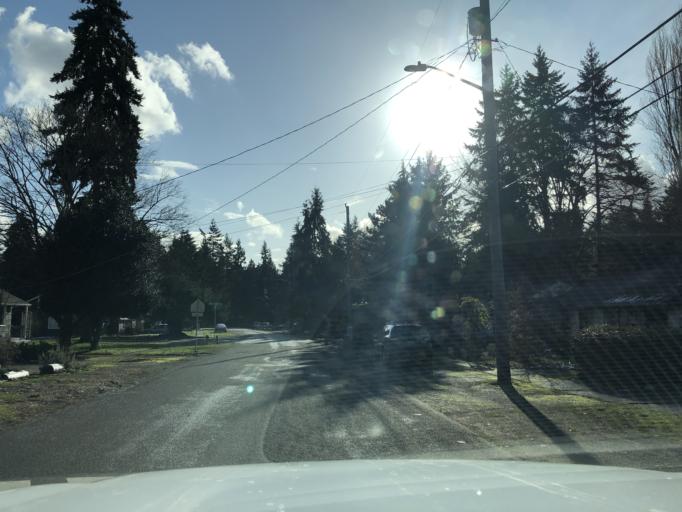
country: US
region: Washington
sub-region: King County
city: Lake Forest Park
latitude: 47.7226
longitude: -122.3046
